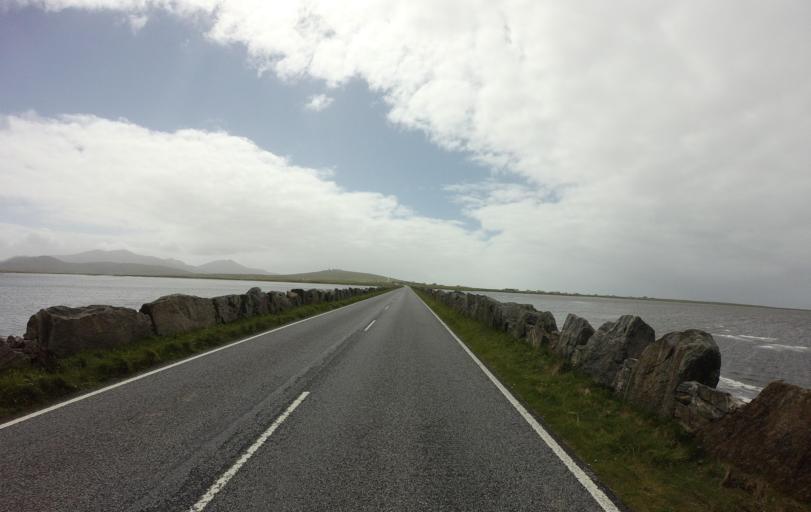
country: GB
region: Scotland
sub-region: Eilean Siar
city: Benbecula
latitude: 57.3622
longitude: -7.3550
